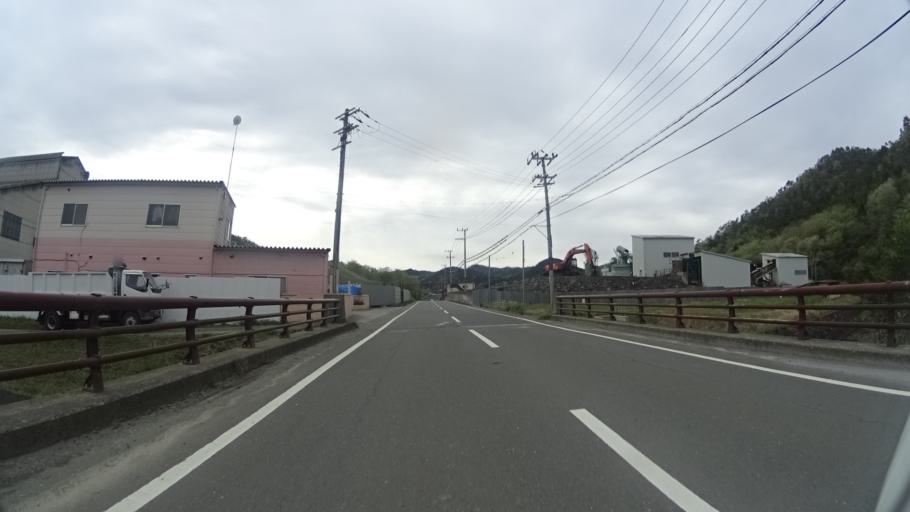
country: JP
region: Kyoto
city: Ayabe
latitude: 35.1854
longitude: 135.4276
